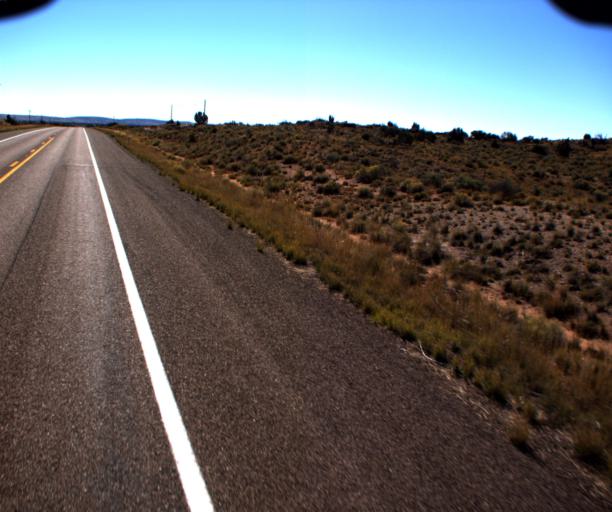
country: US
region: Arizona
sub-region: Apache County
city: Saint Johns
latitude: 34.6269
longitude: -109.6726
